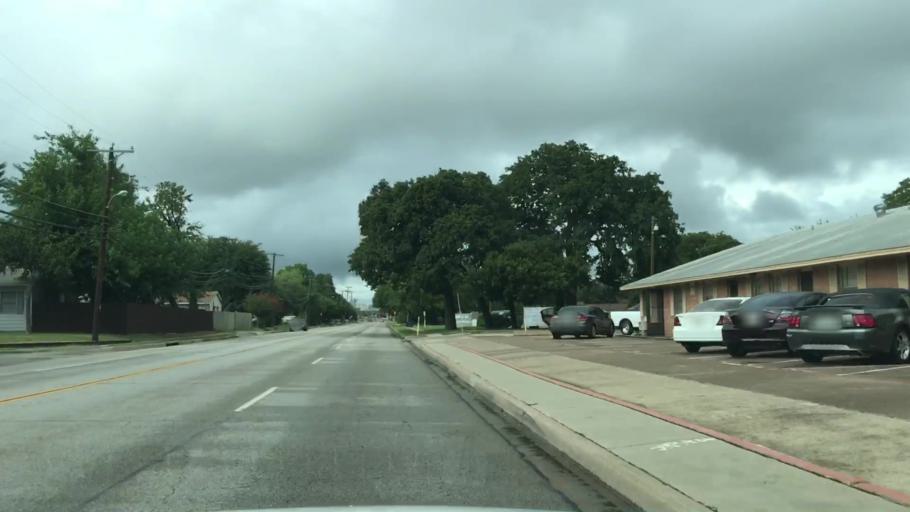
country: US
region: Texas
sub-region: Dallas County
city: Irving
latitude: 32.8310
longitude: -96.9303
